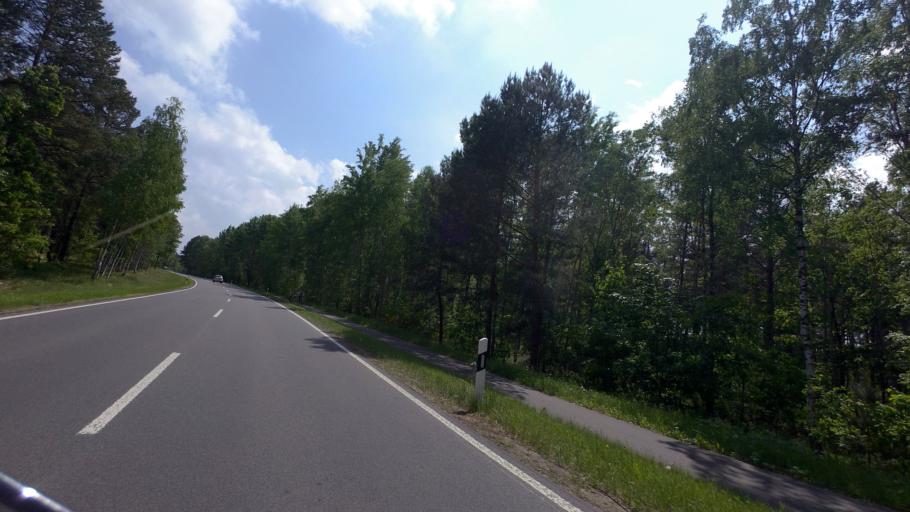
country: DE
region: Saxony
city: Trebendorf
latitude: 51.5286
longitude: 14.6003
